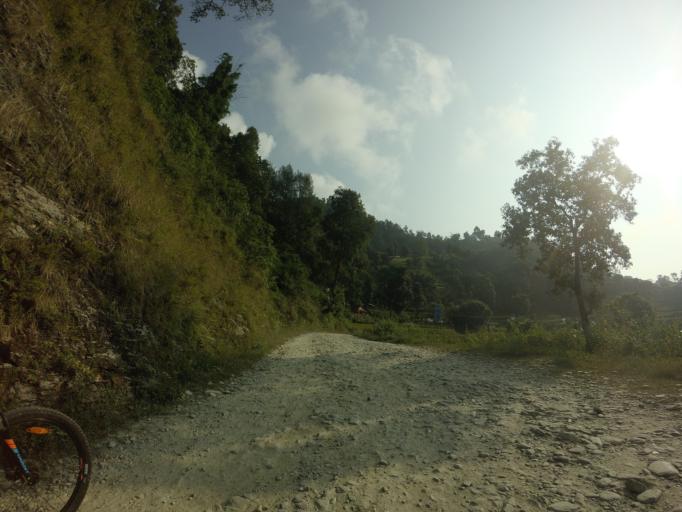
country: NP
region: Western Region
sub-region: Gandaki Zone
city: Pokhara
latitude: 28.2343
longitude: 83.9155
